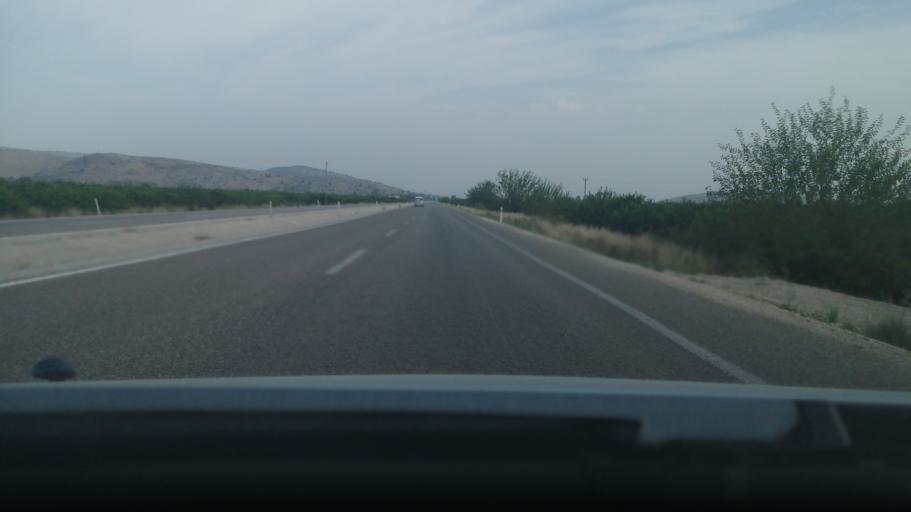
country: TR
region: Adana
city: Kozan
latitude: 37.3853
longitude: 35.8067
